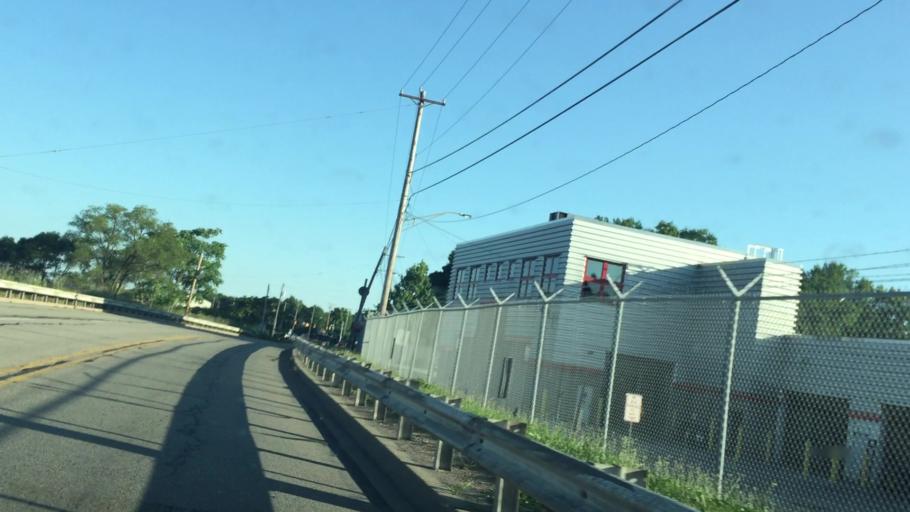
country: US
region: Pennsylvania
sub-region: Allegheny County
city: West View
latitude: 40.5009
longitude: -80.0229
